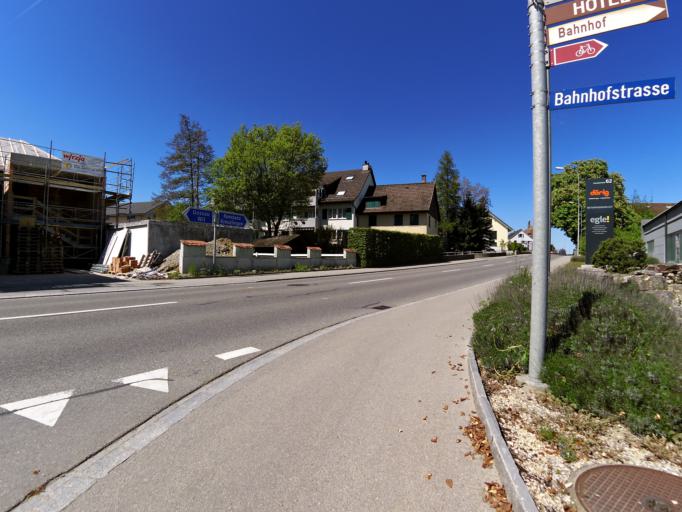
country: CH
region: Thurgau
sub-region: Weinfelden District
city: Berg
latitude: 47.5813
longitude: 9.1679
